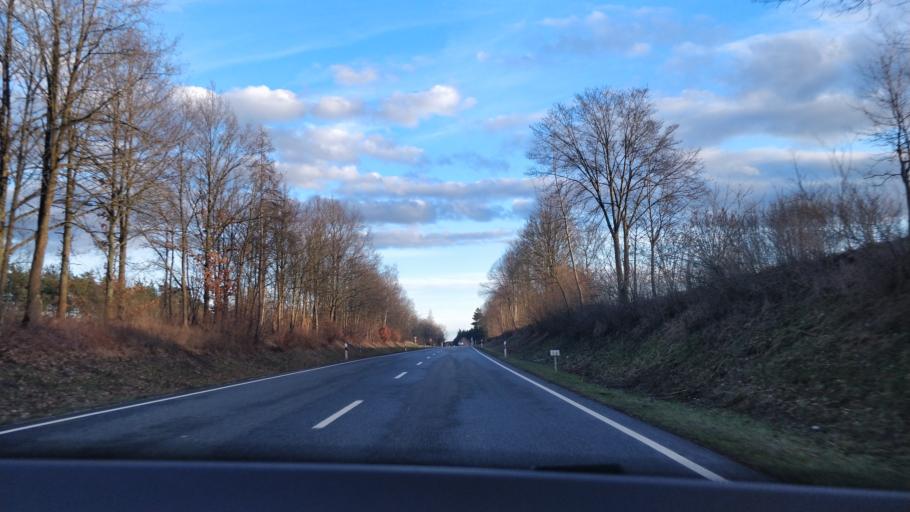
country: DE
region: Bavaria
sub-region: Upper Palatinate
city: Pressath
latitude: 49.7585
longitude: 11.9272
